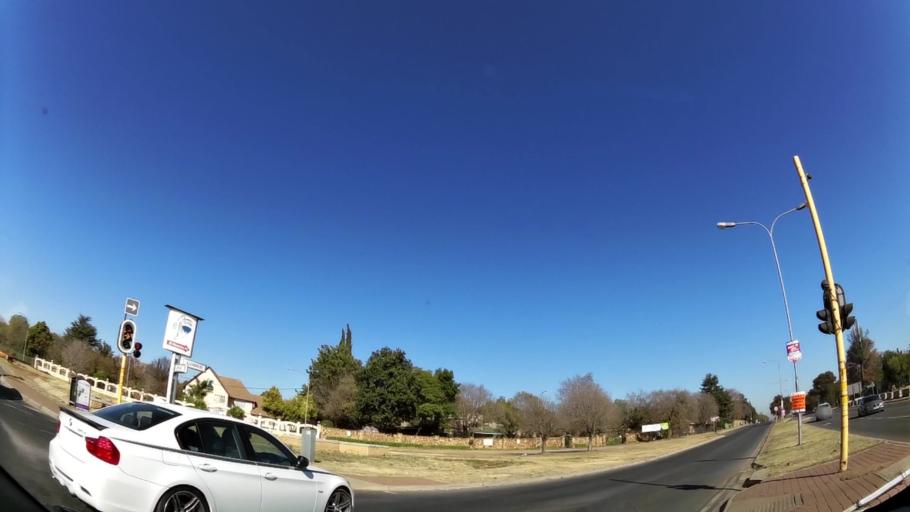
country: ZA
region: Gauteng
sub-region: City of Tshwane Metropolitan Municipality
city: Centurion
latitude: -25.8620
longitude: 28.2213
